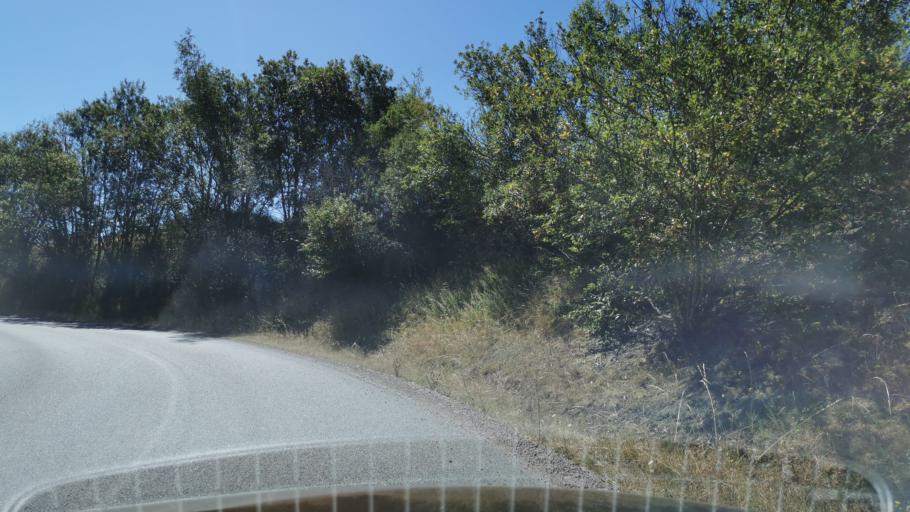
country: FR
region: Bourgogne
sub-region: Departement de Saone-et-Loire
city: Ecuisses
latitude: 46.7385
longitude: 4.5607
